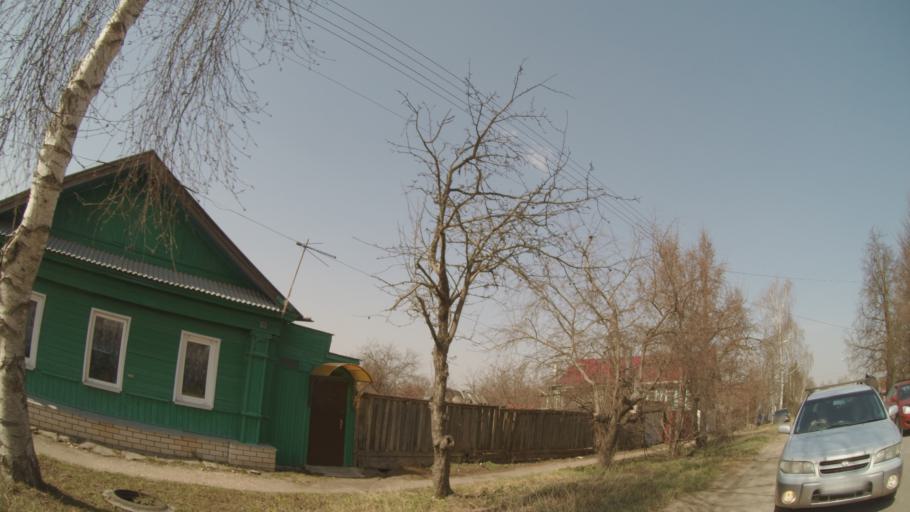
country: RU
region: Nizjnij Novgorod
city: Arzamas
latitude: 55.3879
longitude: 43.8242
